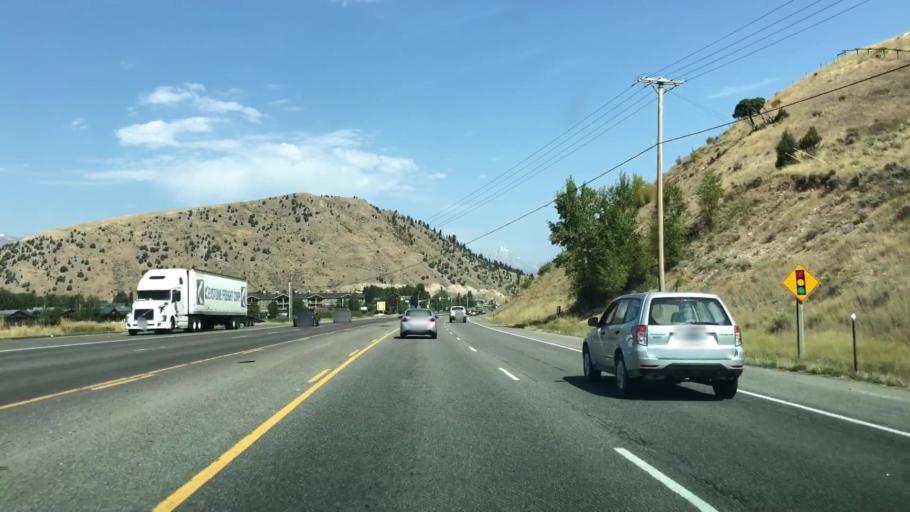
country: US
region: Wyoming
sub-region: Teton County
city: Rafter J Ranch
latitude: 43.4552
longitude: -110.7931
